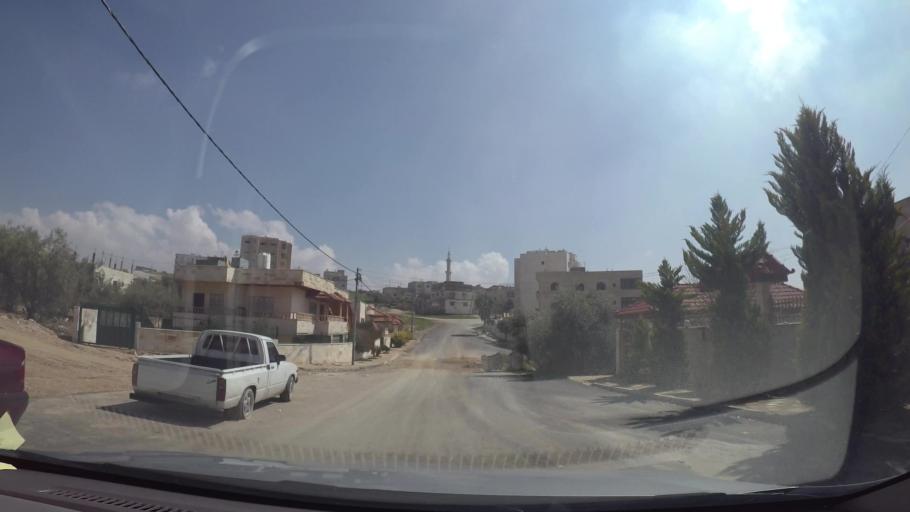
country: JO
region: Amman
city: Al Bunayyat ash Shamaliyah
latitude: 31.8926
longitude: 35.8895
